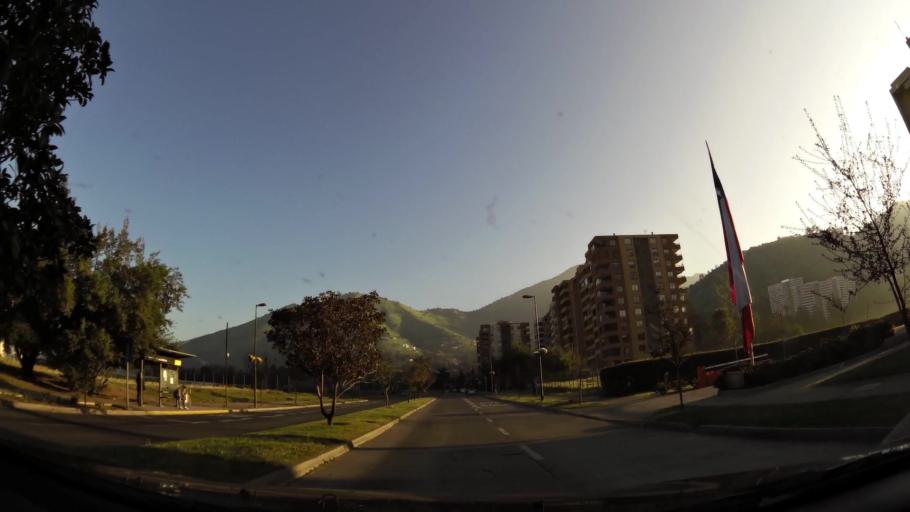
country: CL
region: Santiago Metropolitan
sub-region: Provincia de Santiago
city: Santiago
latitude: -33.3866
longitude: -70.6149
